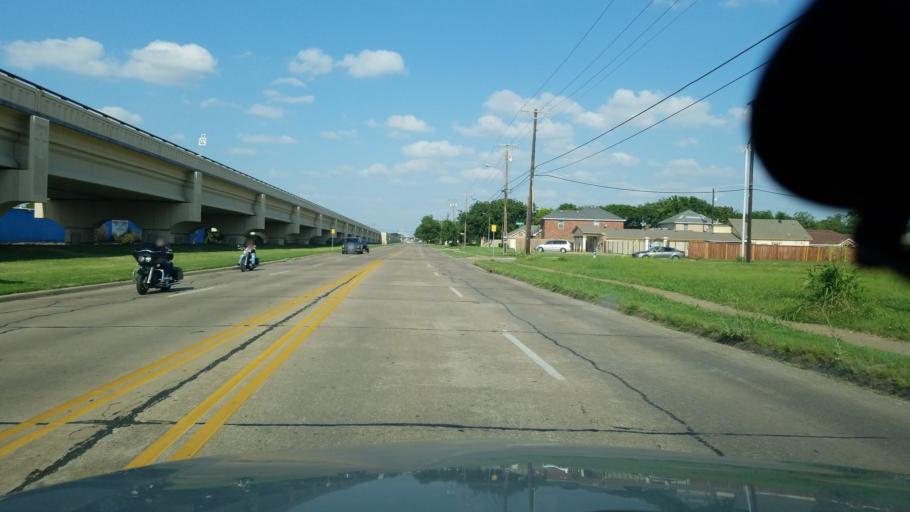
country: US
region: Texas
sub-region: Dallas County
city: Irving
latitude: 32.8153
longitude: -96.9743
